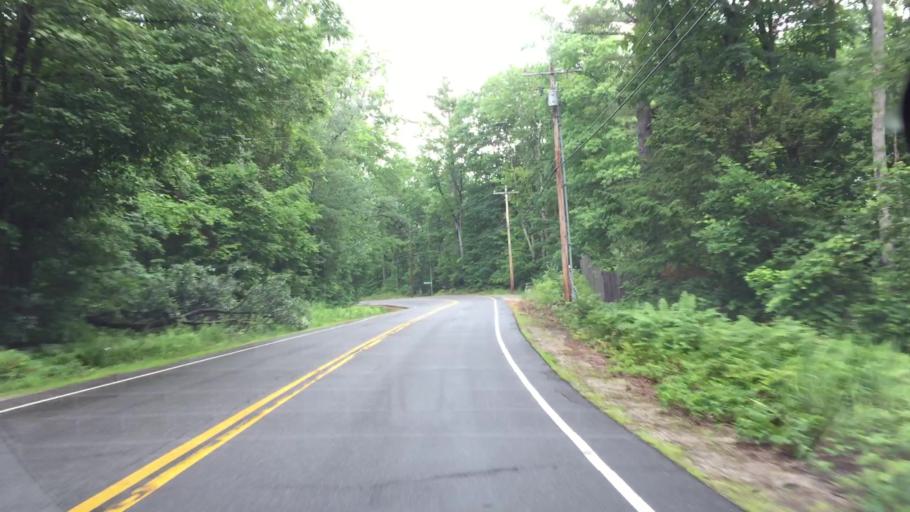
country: US
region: New Hampshire
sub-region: Carroll County
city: Center Harbor
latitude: 43.7373
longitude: -71.4773
